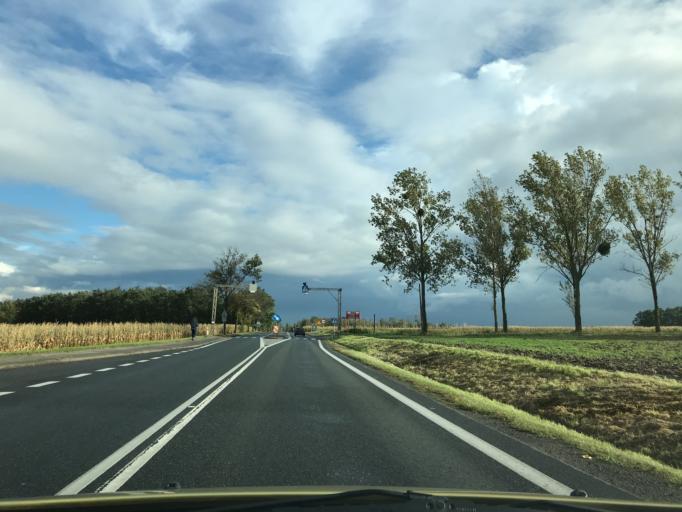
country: PL
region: Greater Poland Voivodeship
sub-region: Kalisz
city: Kalisz
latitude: 51.7762
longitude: 18.0217
